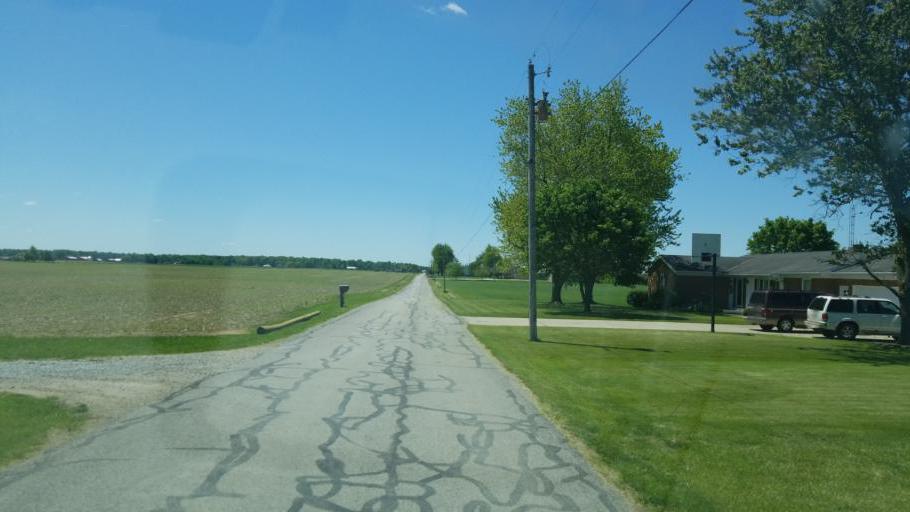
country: US
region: Ohio
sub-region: Shelby County
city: Fort Loramie
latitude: 40.3718
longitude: -84.3166
